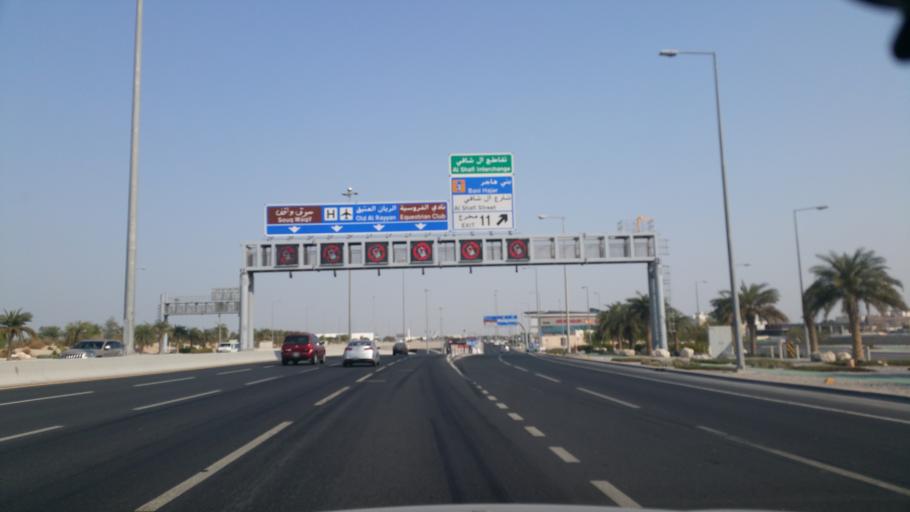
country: QA
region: Baladiyat ar Rayyan
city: Ar Rayyan
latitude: 25.3043
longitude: 51.4175
